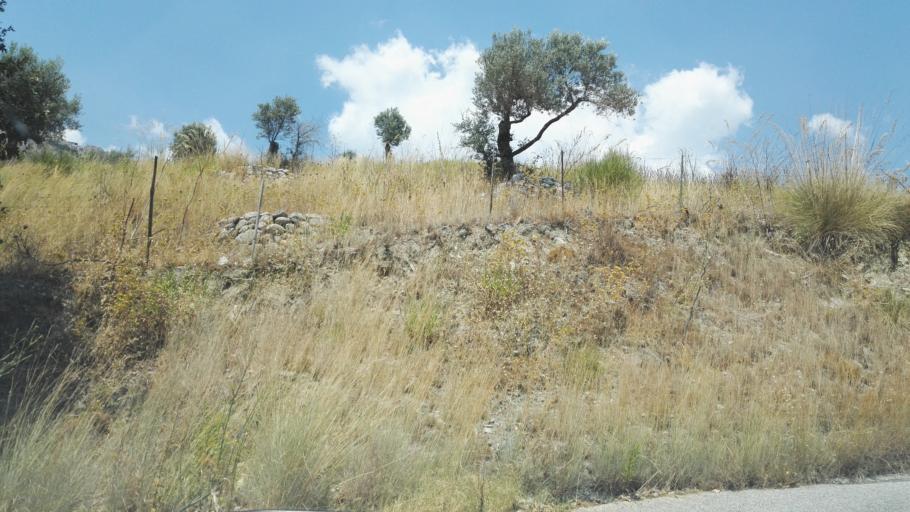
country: IT
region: Calabria
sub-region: Provincia di Reggio Calabria
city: Stilo
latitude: 38.4740
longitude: 16.4724
